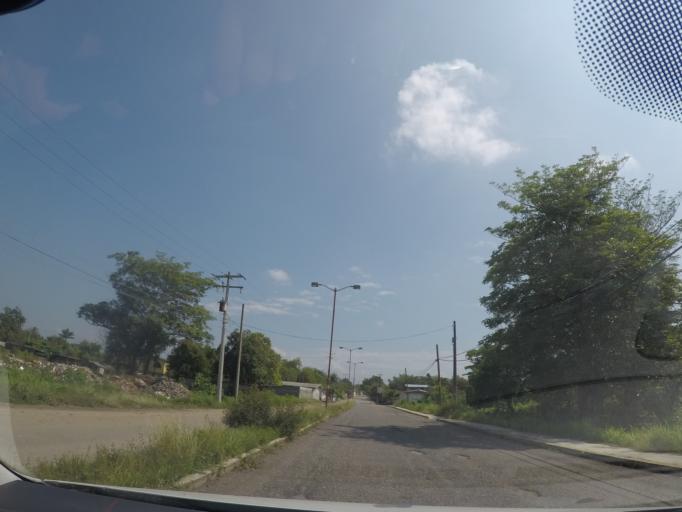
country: MX
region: Oaxaca
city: San Francisco Ixhuatan
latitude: 16.3952
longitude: -94.4584
